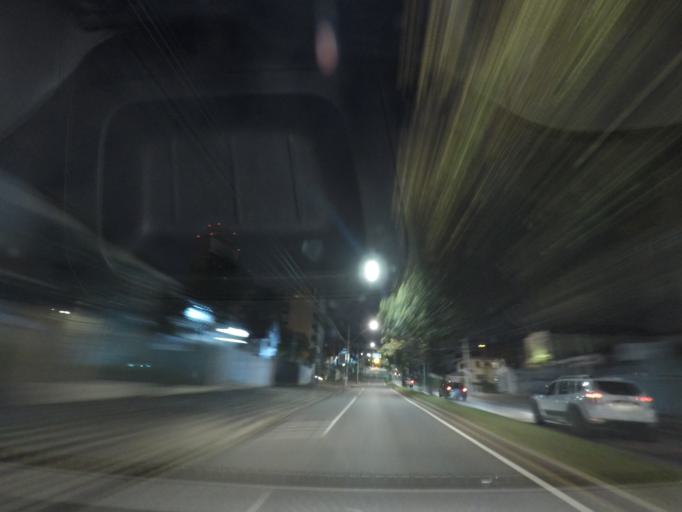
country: BR
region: Parana
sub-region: Curitiba
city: Curitiba
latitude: -25.4234
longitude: -49.2778
